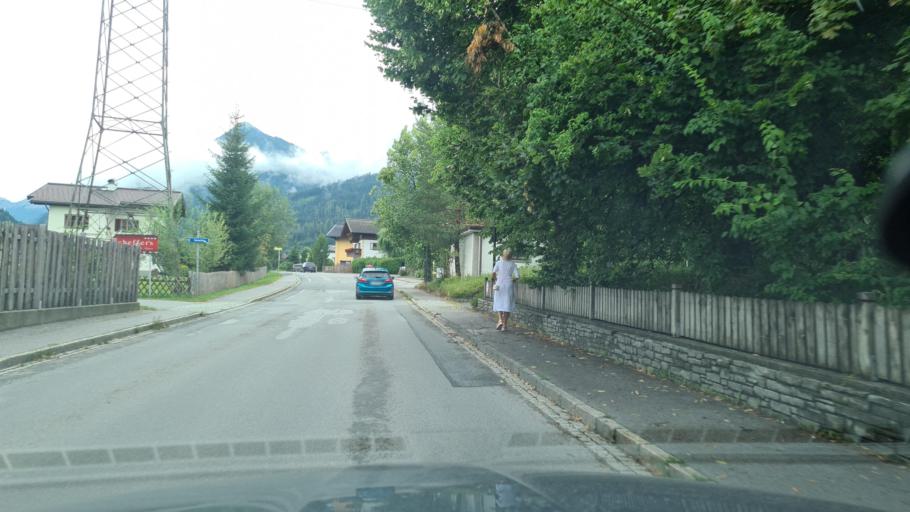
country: AT
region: Salzburg
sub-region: Politischer Bezirk Sankt Johann im Pongau
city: Altenmarkt im Pongau
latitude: 47.3741
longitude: 13.4214
